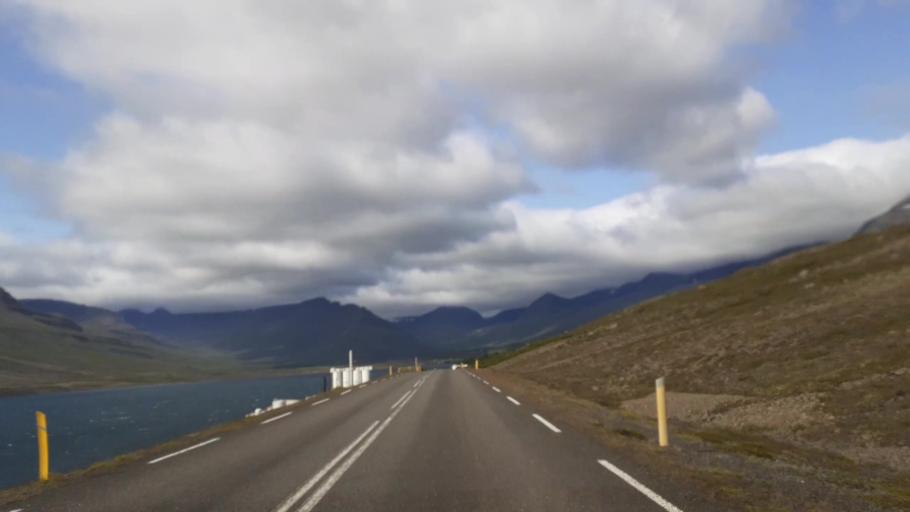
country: IS
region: East
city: Eskifjoerdur
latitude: 64.9231
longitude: -13.9775
